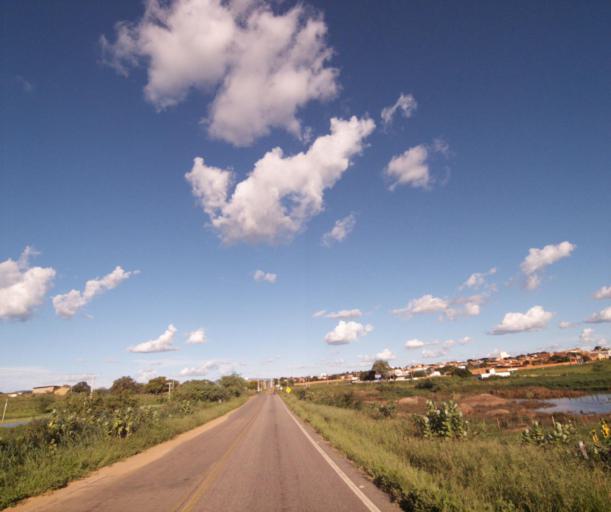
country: BR
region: Bahia
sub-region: Guanambi
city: Guanambi
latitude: -14.2119
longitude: -42.8065
